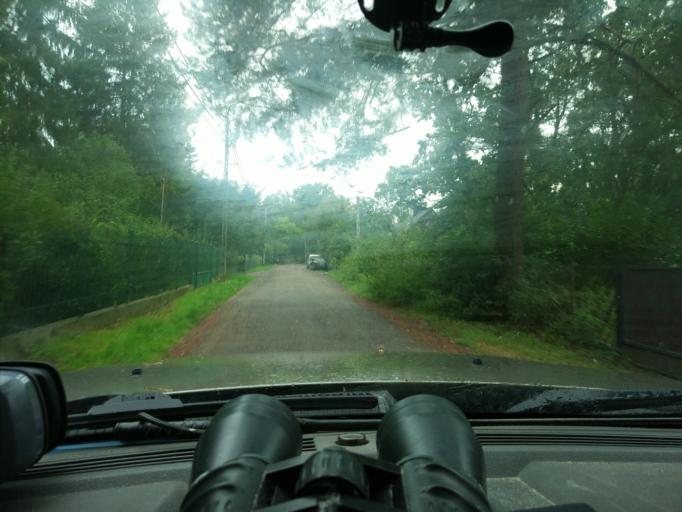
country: PL
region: Masovian Voivodeship
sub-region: Powiat grodziski
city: Podkowa Lesna
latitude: 52.1281
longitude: 20.7359
